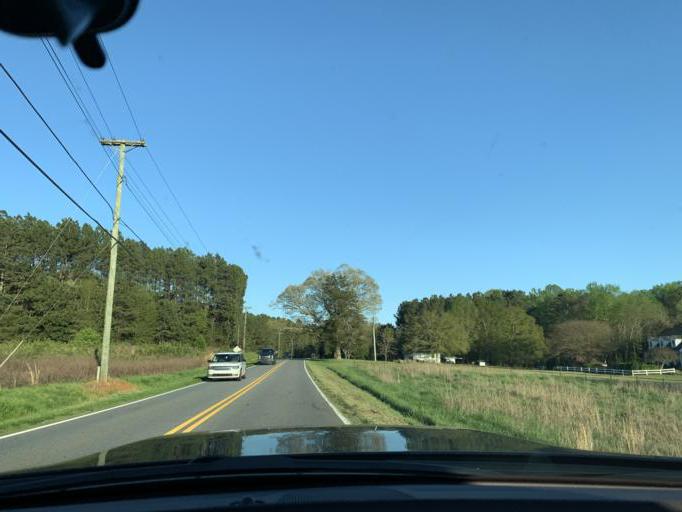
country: US
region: Georgia
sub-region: Forsyth County
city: Cumming
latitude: 34.2510
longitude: -84.1959
